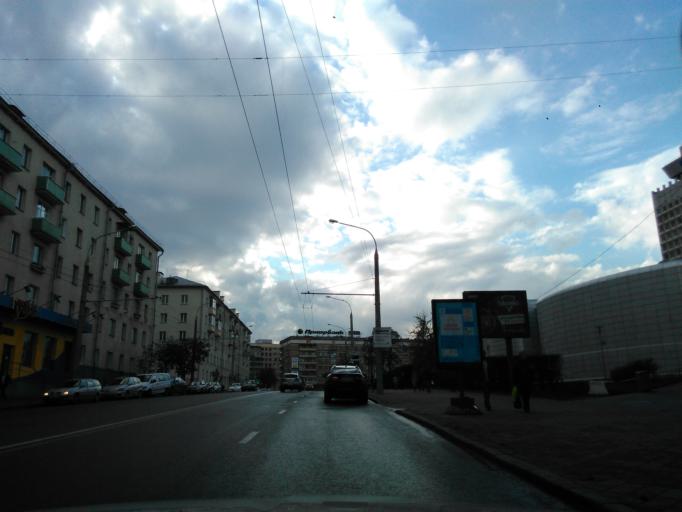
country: BY
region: Minsk
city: Minsk
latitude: 53.9042
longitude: 27.5434
